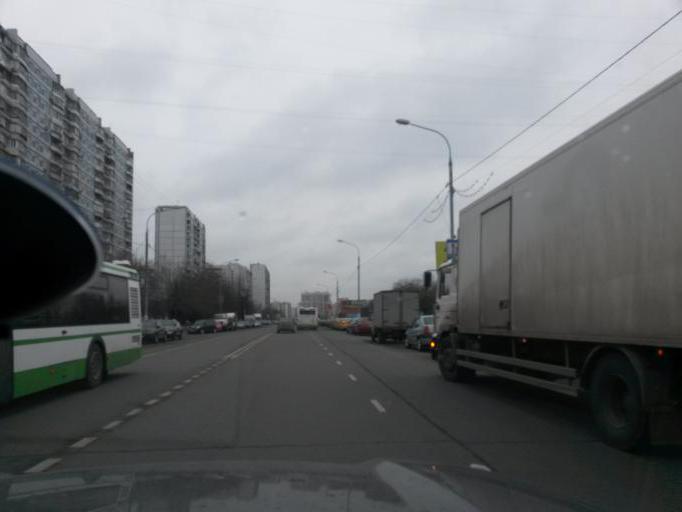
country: RU
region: Moscow
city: Brateyevo
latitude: 55.6352
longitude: 37.7609
